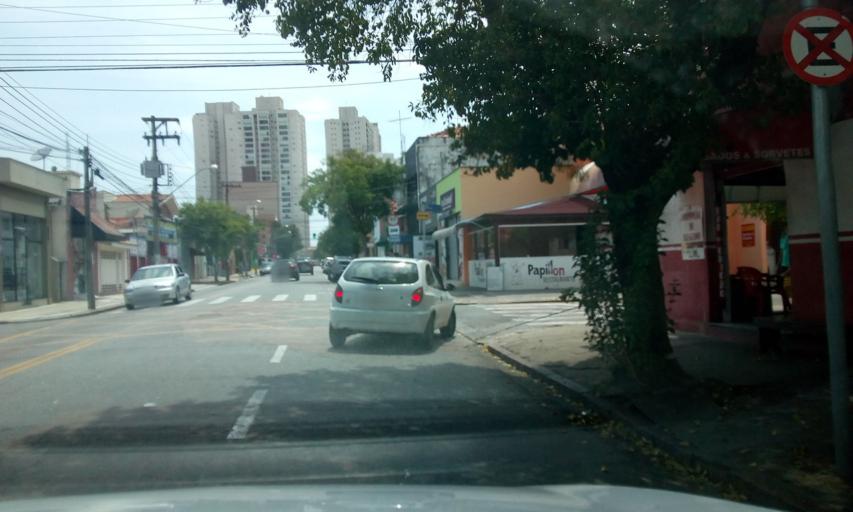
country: BR
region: Sao Paulo
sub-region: Jundiai
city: Jundiai
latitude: -23.2003
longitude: -46.8813
